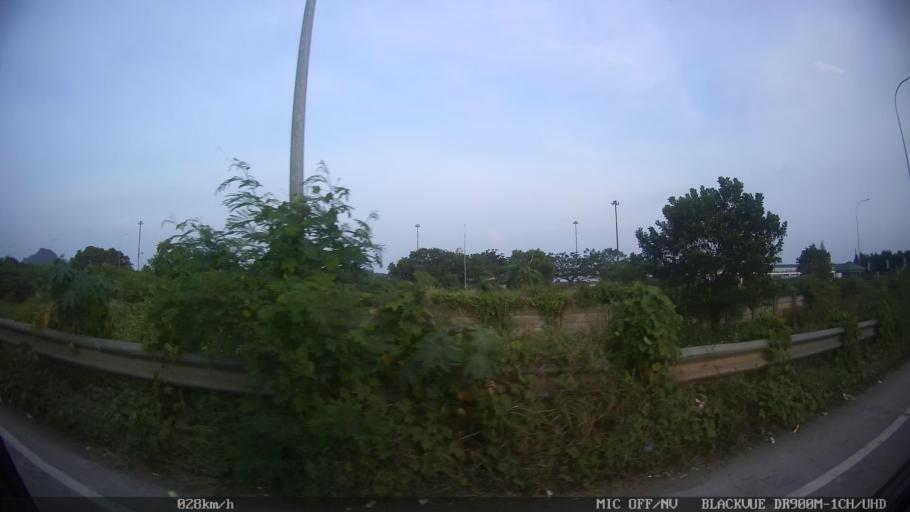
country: ID
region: Lampung
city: Penengahan
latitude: -5.8713
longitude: 105.7501
